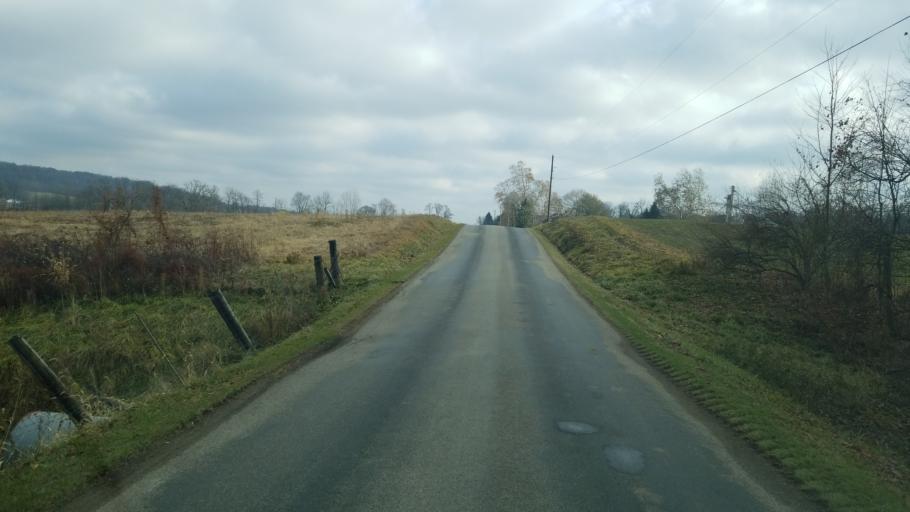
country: US
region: Ohio
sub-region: Richland County
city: Lincoln Heights
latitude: 40.8276
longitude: -82.4722
